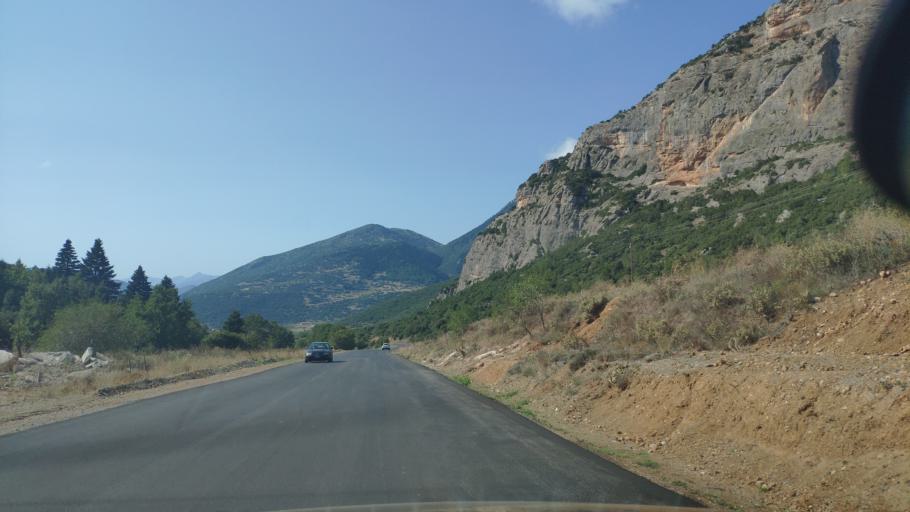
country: GR
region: Peloponnese
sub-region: Nomos Korinthias
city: Nemea
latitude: 37.9363
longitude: 22.5386
